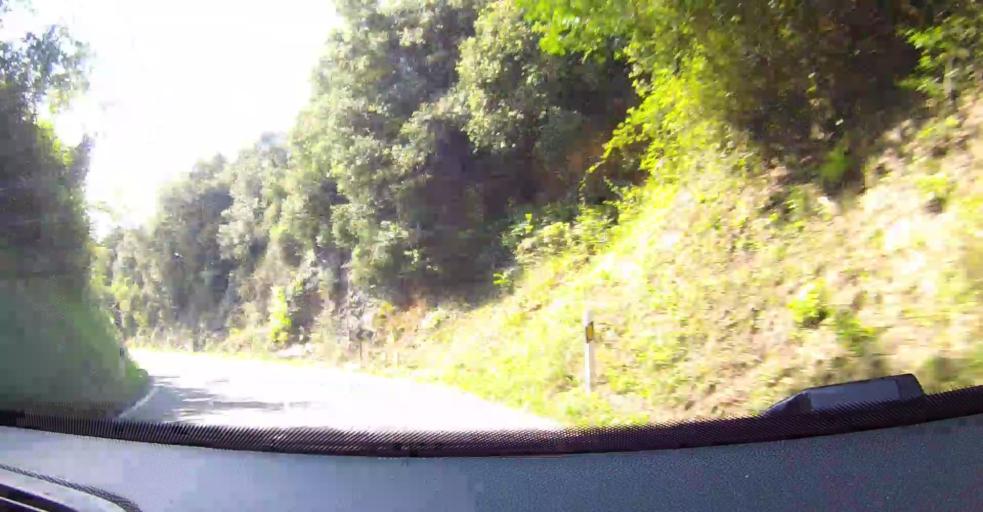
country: ES
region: Basque Country
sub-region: Bizkaia
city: Kortezubi
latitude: 43.3607
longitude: -2.6481
